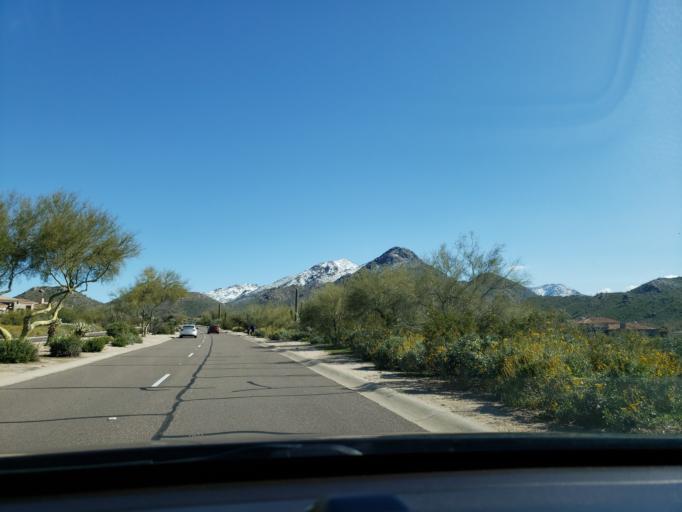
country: US
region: Arizona
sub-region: Maricopa County
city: Carefree
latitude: 33.7080
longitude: -111.8475
